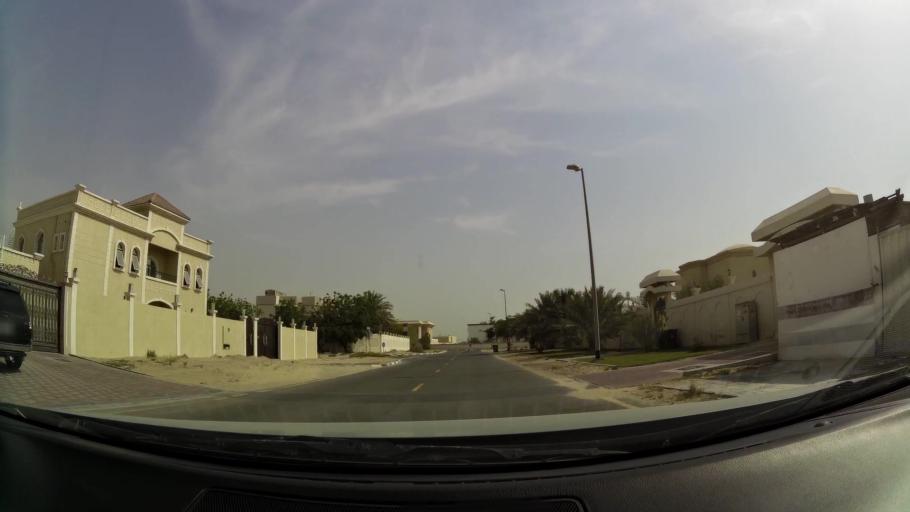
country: AE
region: Ash Shariqah
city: Sharjah
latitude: 25.2532
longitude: 55.4386
